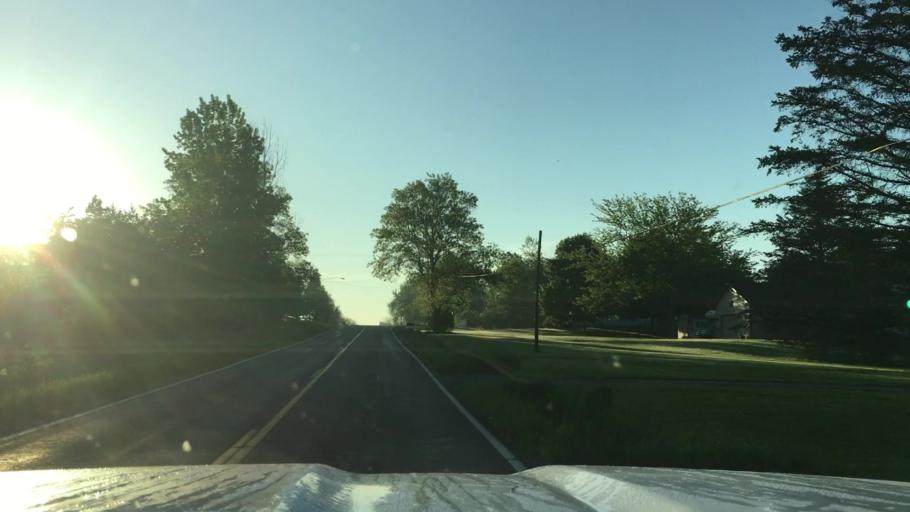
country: US
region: Michigan
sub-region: Kent County
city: Byron Center
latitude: 42.7829
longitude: -85.7441
